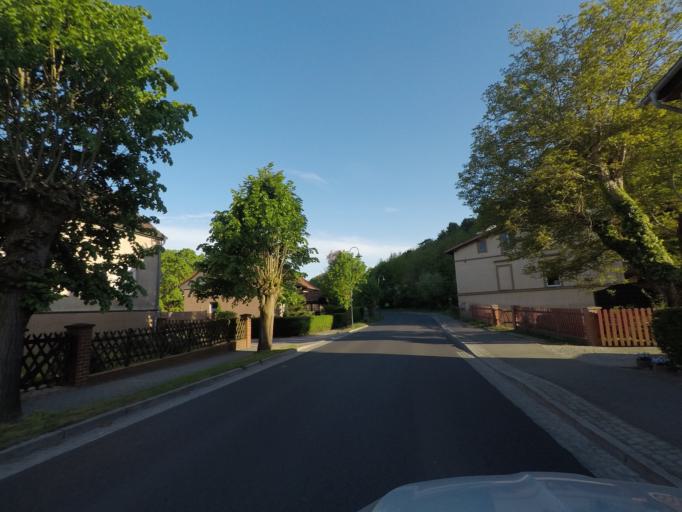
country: DE
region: Brandenburg
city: Falkenberg
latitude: 52.8010
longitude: 13.9613
